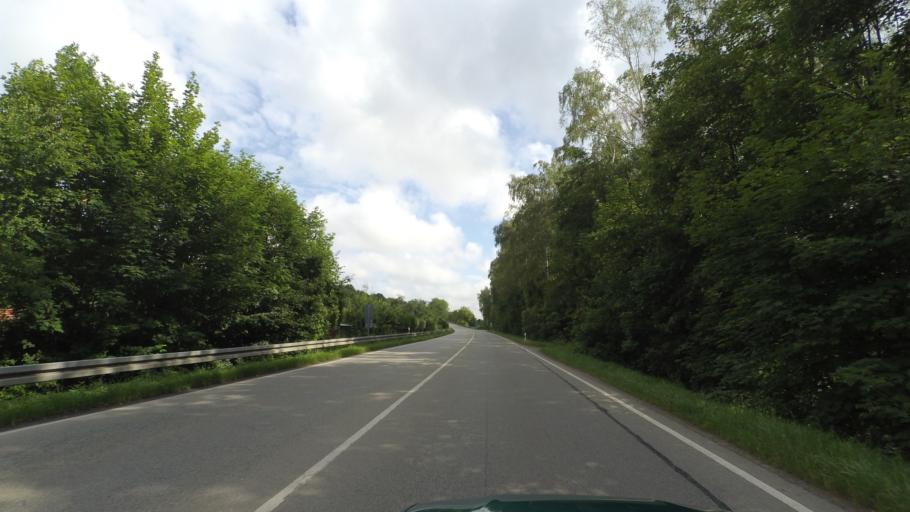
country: DE
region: Bavaria
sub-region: Lower Bavaria
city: Straubing
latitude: 48.8924
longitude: 12.5788
